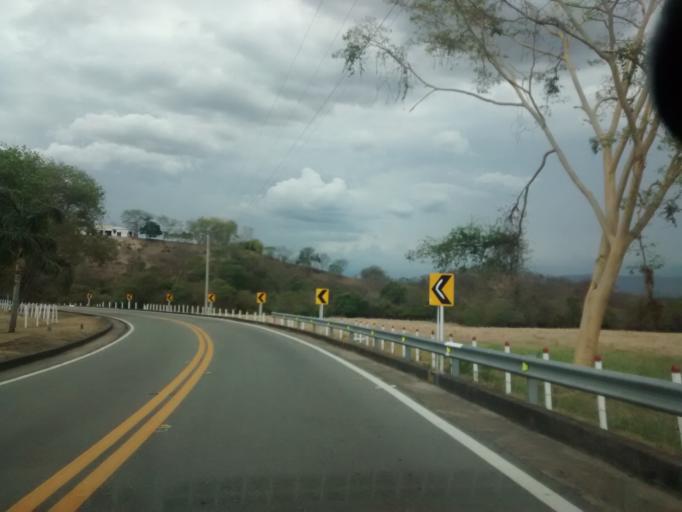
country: CO
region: Cundinamarca
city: Agua de Dios
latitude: 4.4095
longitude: -74.7103
